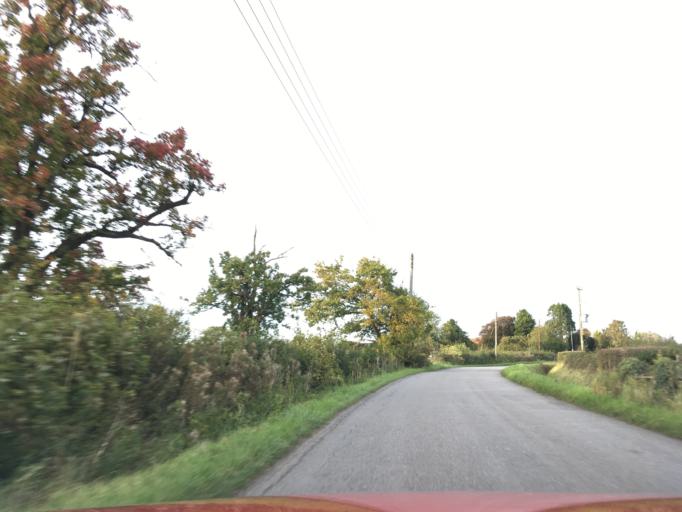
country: GB
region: England
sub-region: South Gloucestershire
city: Severn Beach
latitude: 51.5729
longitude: -2.6359
